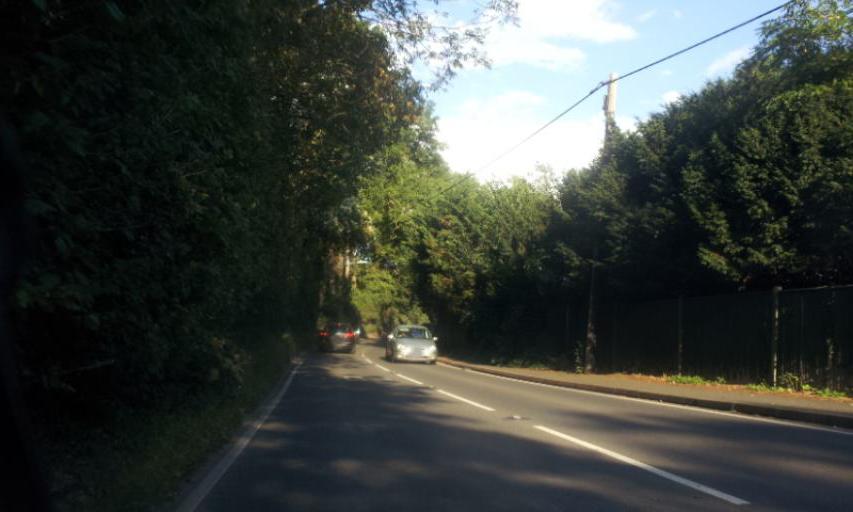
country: GB
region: England
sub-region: Kent
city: Longfield
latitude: 51.3933
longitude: 0.3210
